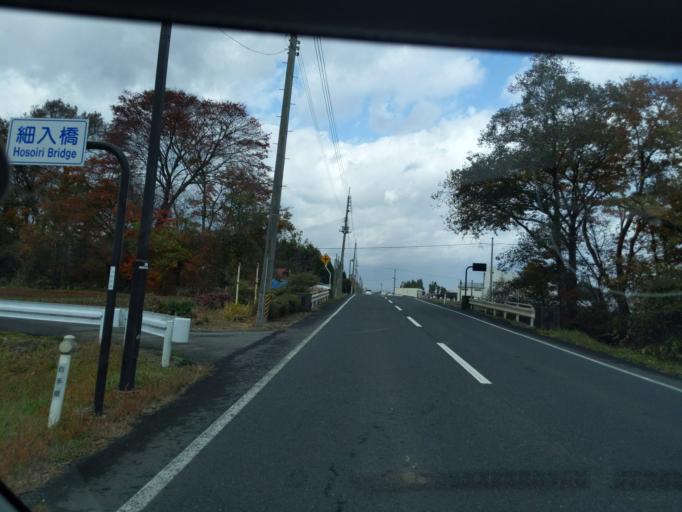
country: JP
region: Iwate
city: Mizusawa
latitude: 39.0819
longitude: 141.0514
